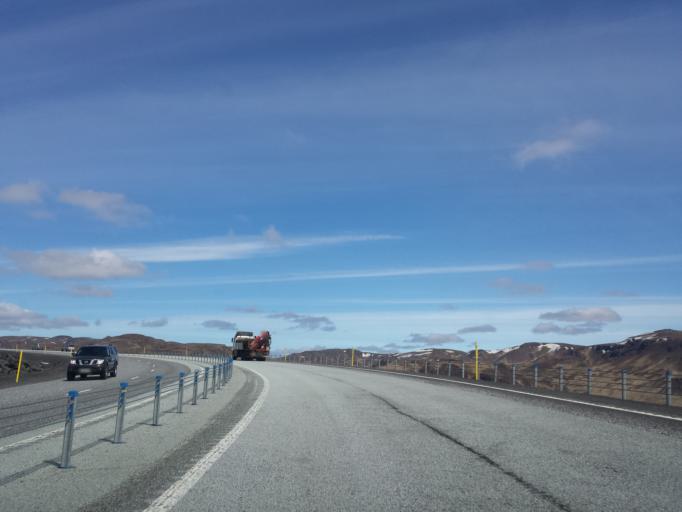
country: IS
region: South
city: Hveragerdi
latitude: 64.0062
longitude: -21.2173
